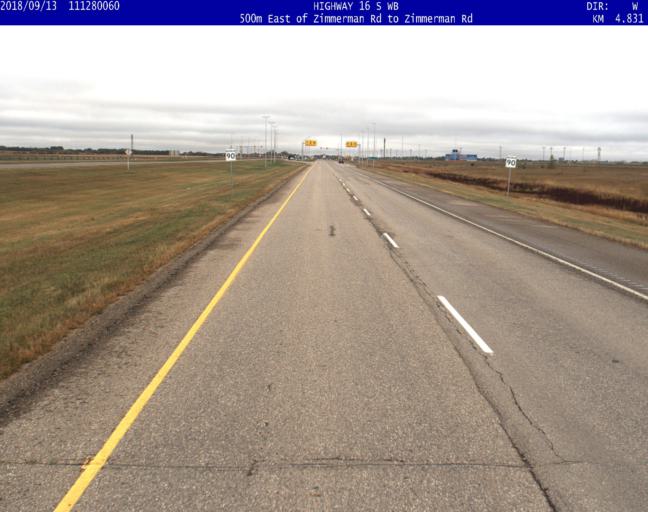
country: CA
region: Saskatchewan
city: Saskatoon
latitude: 52.0862
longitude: -106.5281
